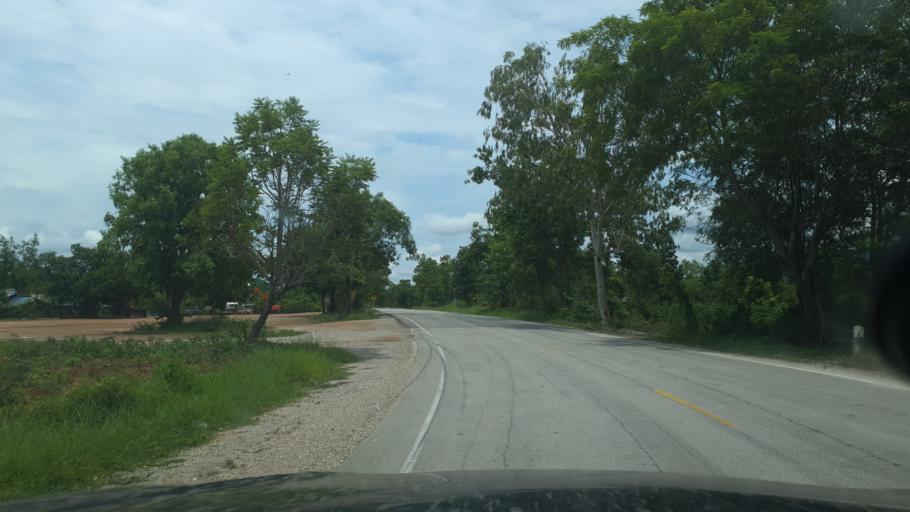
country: TH
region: Lampang
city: Sop Prap
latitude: 17.9135
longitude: 99.3975
